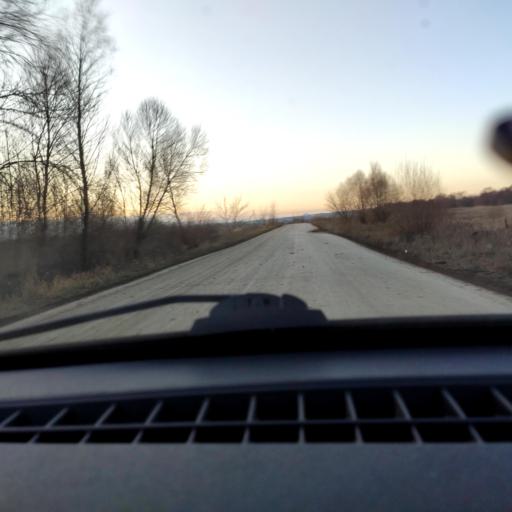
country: RU
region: Bashkortostan
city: Ufa
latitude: 54.7018
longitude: 56.1218
